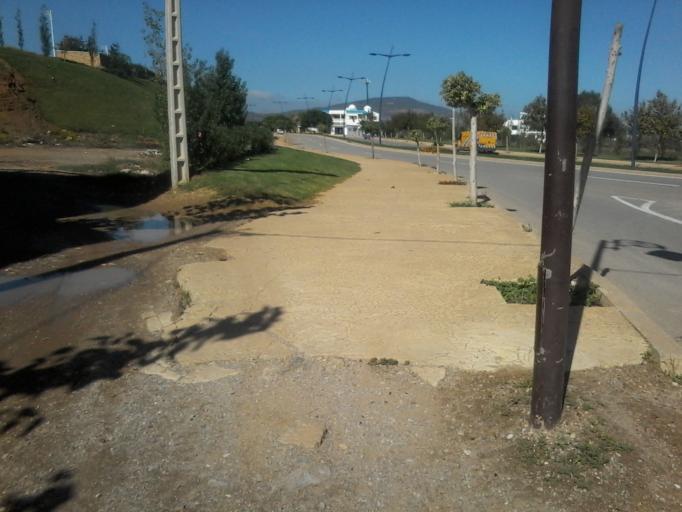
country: MA
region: Tanger-Tetouan
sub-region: Tetouan
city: Martil
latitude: 35.6937
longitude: -5.3329
